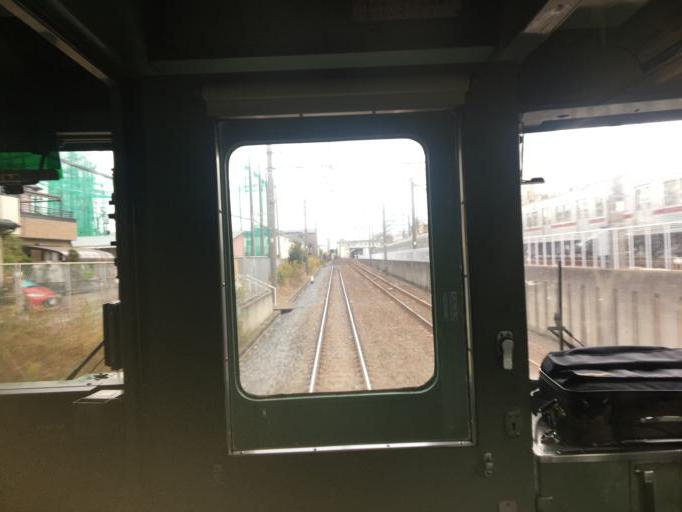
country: JP
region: Saitama
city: Wako
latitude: 35.7904
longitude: 139.6082
